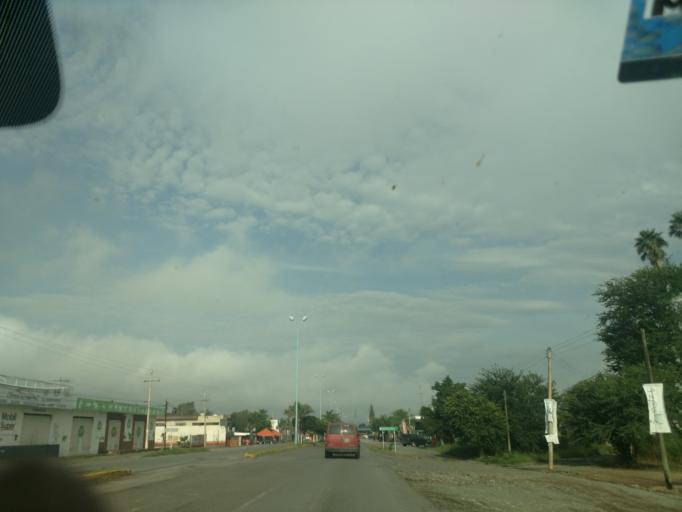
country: MX
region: Jalisco
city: Ameca
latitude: 20.5373
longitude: -104.0381
